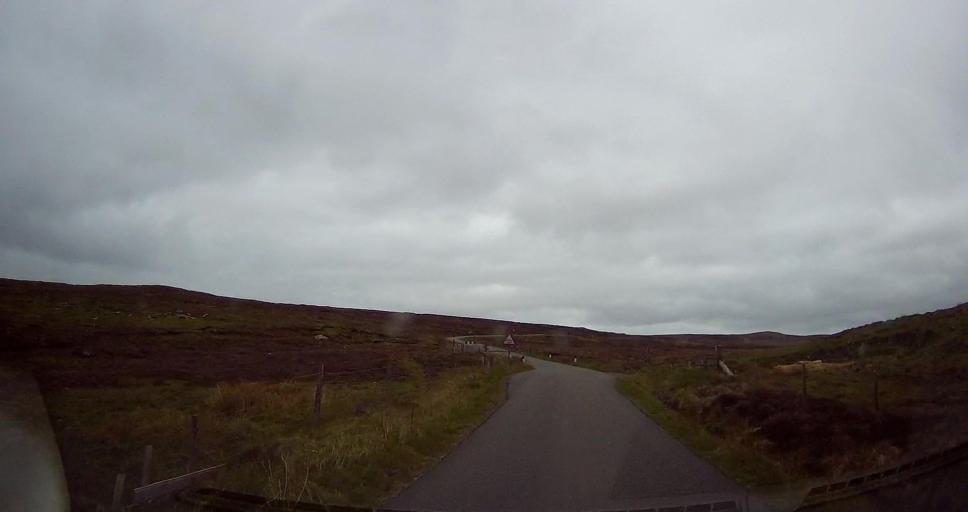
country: GB
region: Scotland
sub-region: Shetland Islands
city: Lerwick
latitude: 60.3110
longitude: -1.3391
